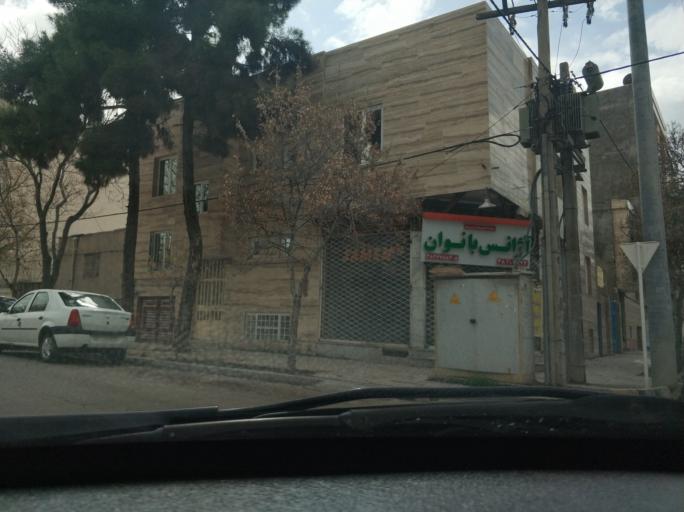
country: IR
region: Razavi Khorasan
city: Mashhad
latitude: 36.2780
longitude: 59.5708
